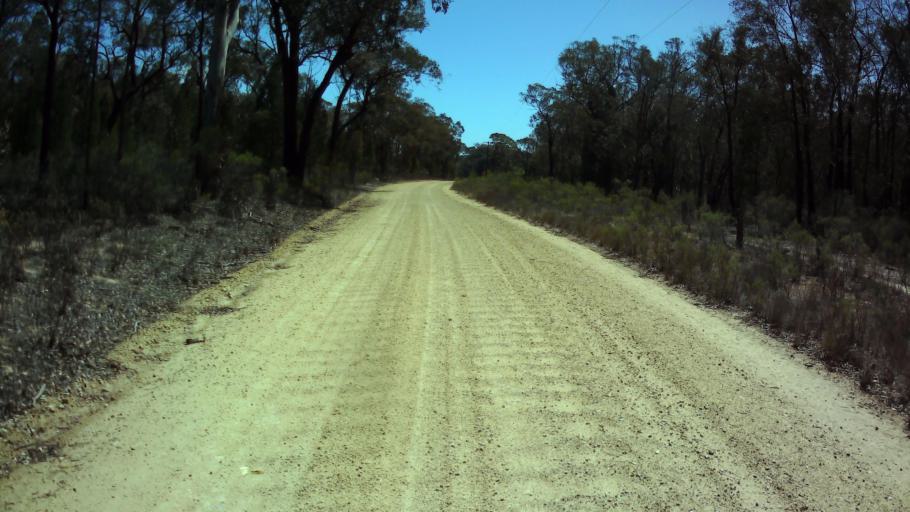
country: AU
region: New South Wales
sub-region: Cowra
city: Cowra
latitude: -33.8415
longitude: 148.4518
